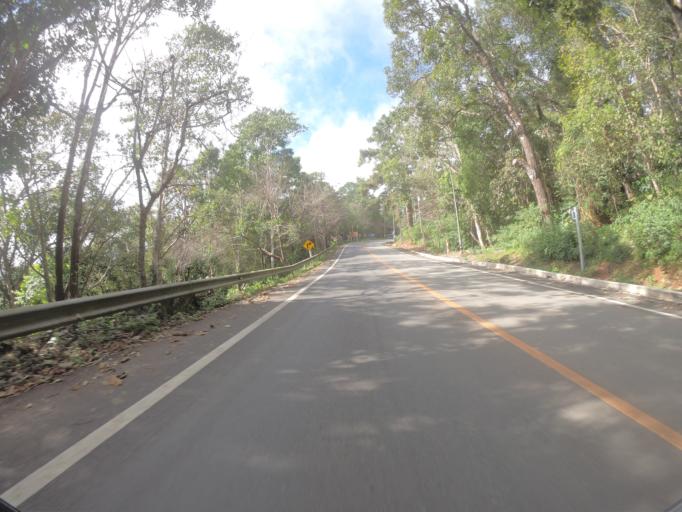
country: TH
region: Chiang Mai
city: Chiang Mai
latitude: 18.8022
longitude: 98.8985
